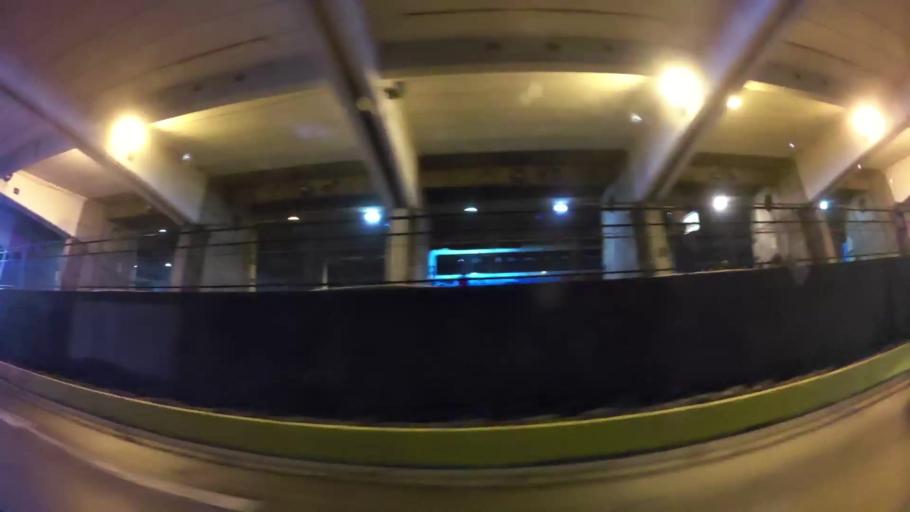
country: CL
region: Santiago Metropolitan
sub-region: Provincia de Santiago
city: Villa Presidente Frei, Nunoa, Santiago, Chile
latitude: -33.5199
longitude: -70.5985
